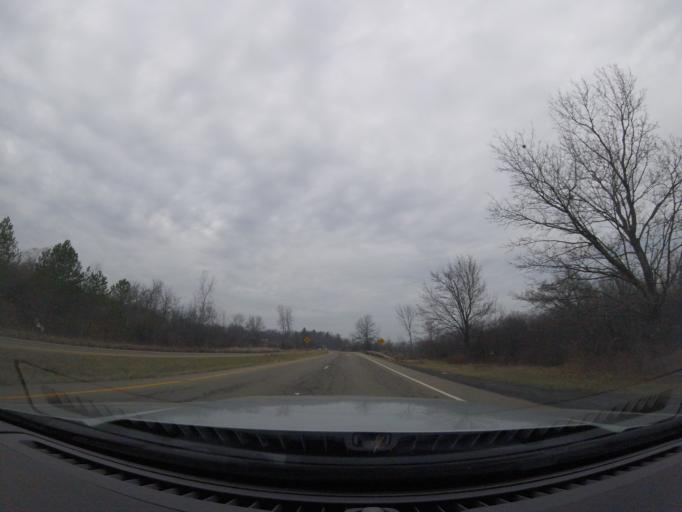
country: US
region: New York
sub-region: Schuyler County
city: Watkins Glen
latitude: 42.4220
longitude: -76.9040
